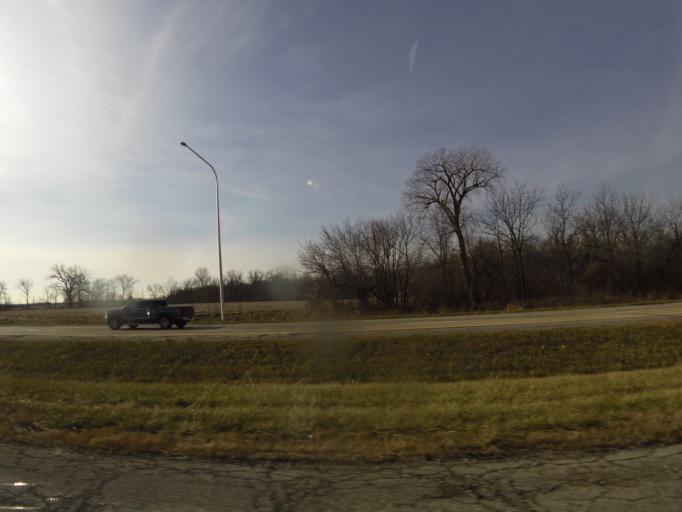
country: US
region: Illinois
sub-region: De Witt County
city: Clinton
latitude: 40.1293
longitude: -88.9672
